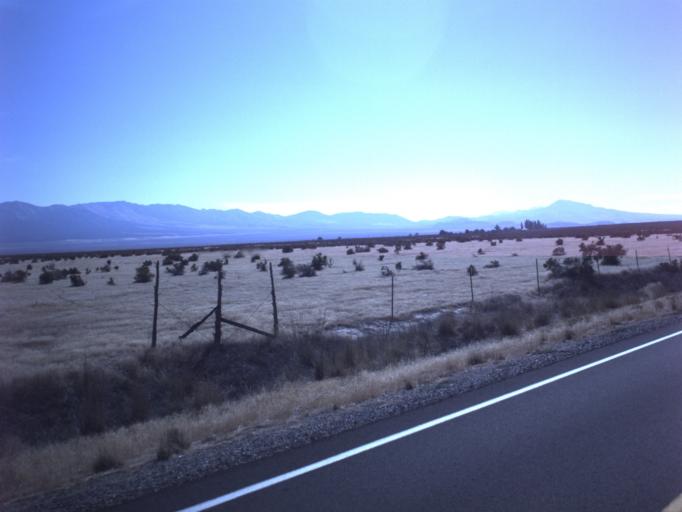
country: US
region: Utah
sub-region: Tooele County
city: Grantsville
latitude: 40.3174
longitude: -112.7437
